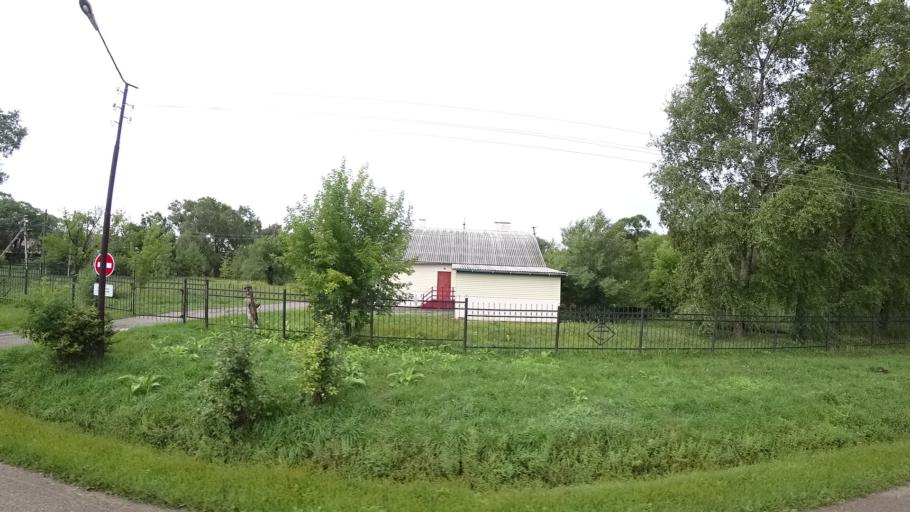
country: RU
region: Primorskiy
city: Chernigovka
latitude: 44.3416
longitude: 132.5826
